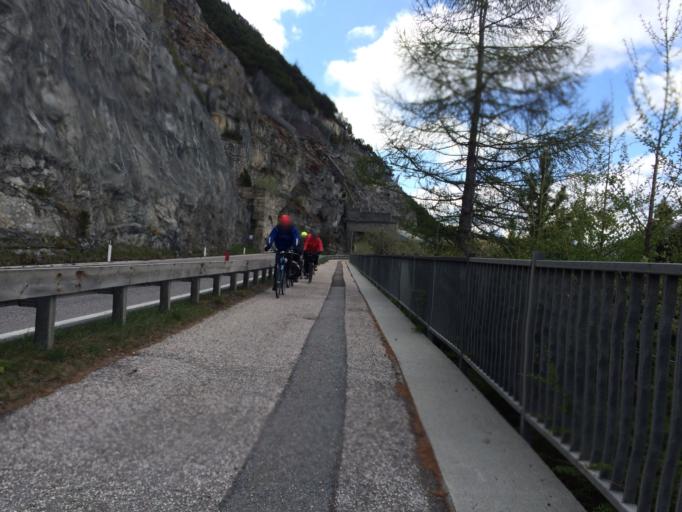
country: IT
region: Trentino-Alto Adige
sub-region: Bolzano
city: Curon Venosta
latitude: 46.7940
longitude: 10.5414
